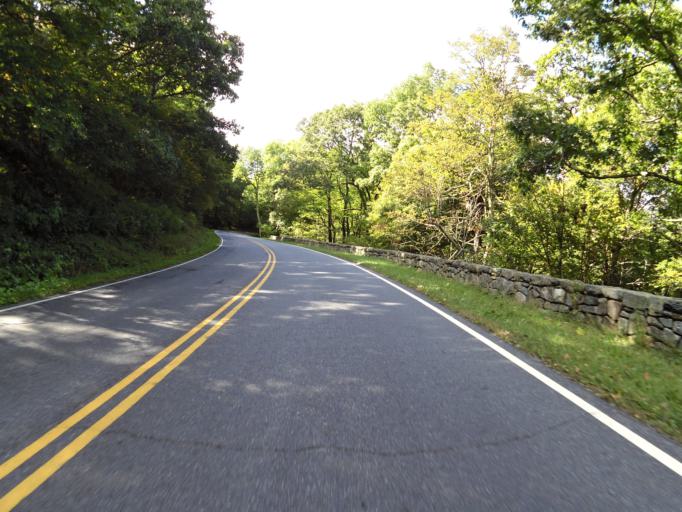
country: US
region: Virginia
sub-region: Page County
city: Stanley
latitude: 38.5703
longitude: -78.3784
